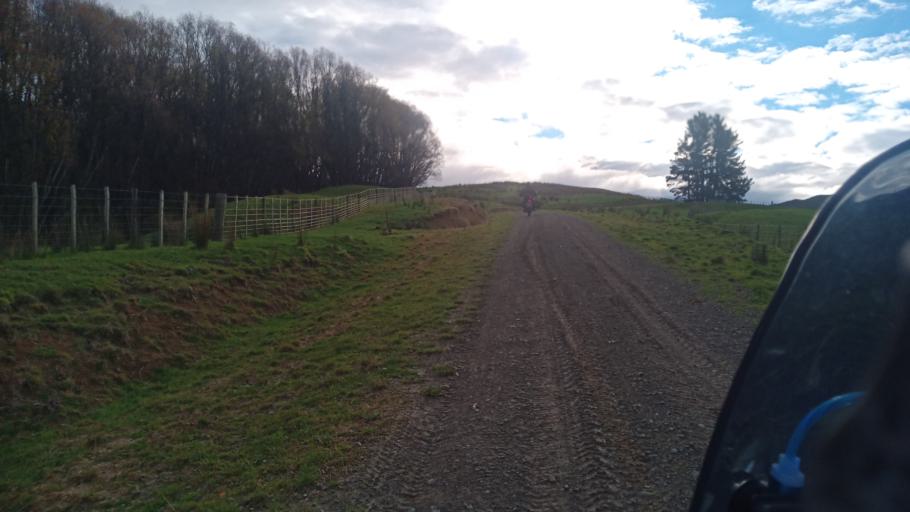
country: NZ
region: Gisborne
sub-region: Gisborne District
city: Gisborne
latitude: -38.3508
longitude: 177.9358
